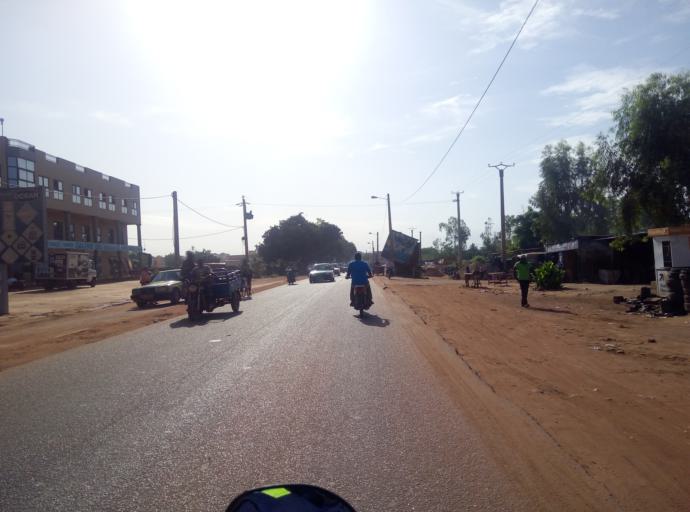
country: ML
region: Bamako
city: Bamako
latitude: 12.6531
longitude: -7.9391
